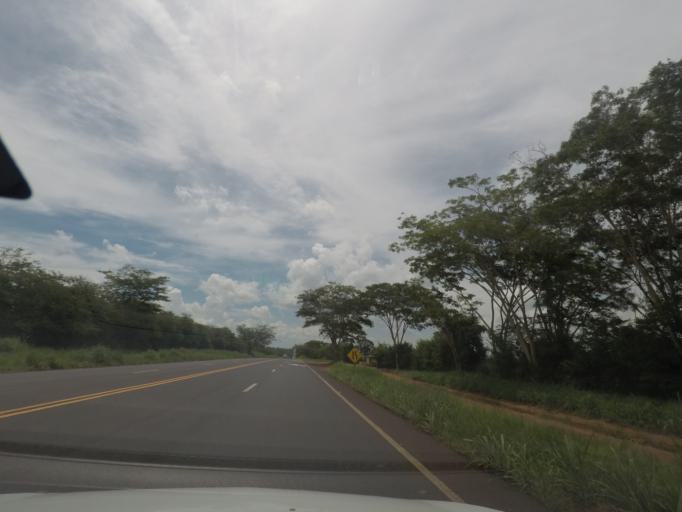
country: BR
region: Sao Paulo
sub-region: Barretos
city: Barretos
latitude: -20.4185
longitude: -48.6313
